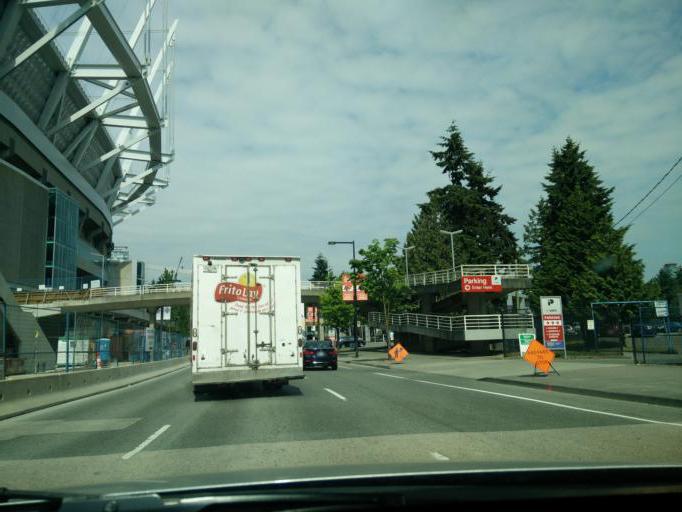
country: CA
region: British Columbia
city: West End
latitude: 49.2752
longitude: -123.1122
